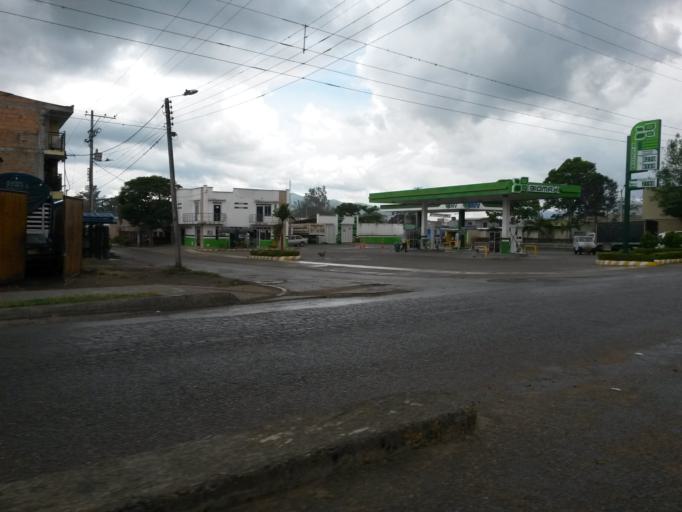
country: CO
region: Huila
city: Pitalito
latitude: 1.8466
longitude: -76.0652
